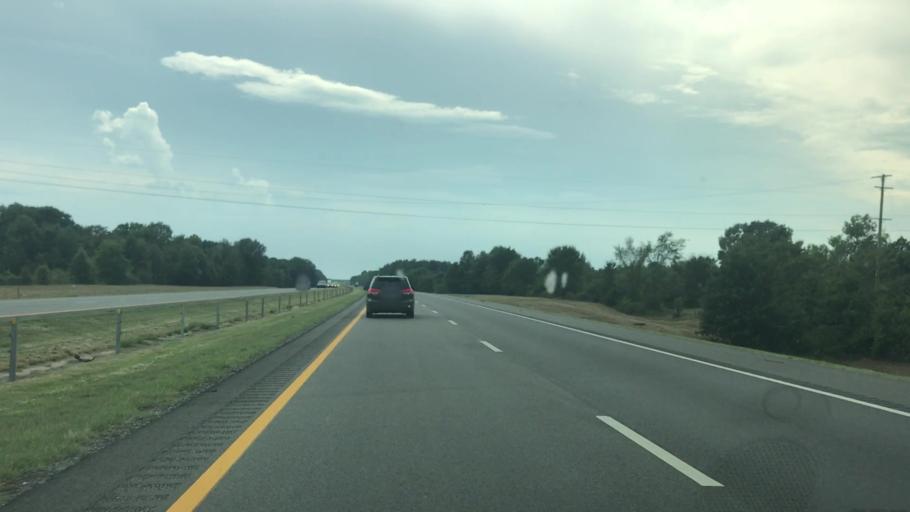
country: US
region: Arkansas
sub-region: Monroe County
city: Brinkley
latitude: 34.8980
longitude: -91.2424
